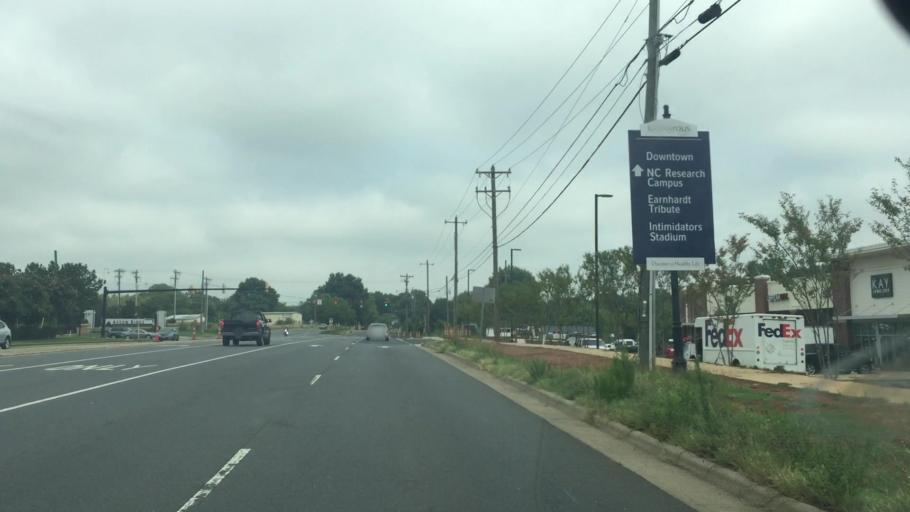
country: US
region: North Carolina
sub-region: Cabarrus County
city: Kannapolis
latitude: 35.4213
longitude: -80.6756
